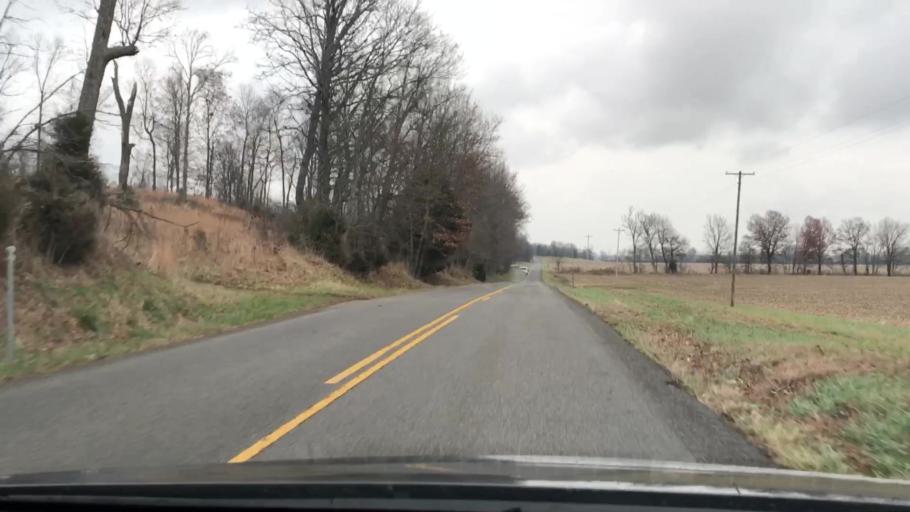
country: US
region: Kentucky
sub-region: Webster County
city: Sebree
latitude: 37.4959
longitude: -87.4475
